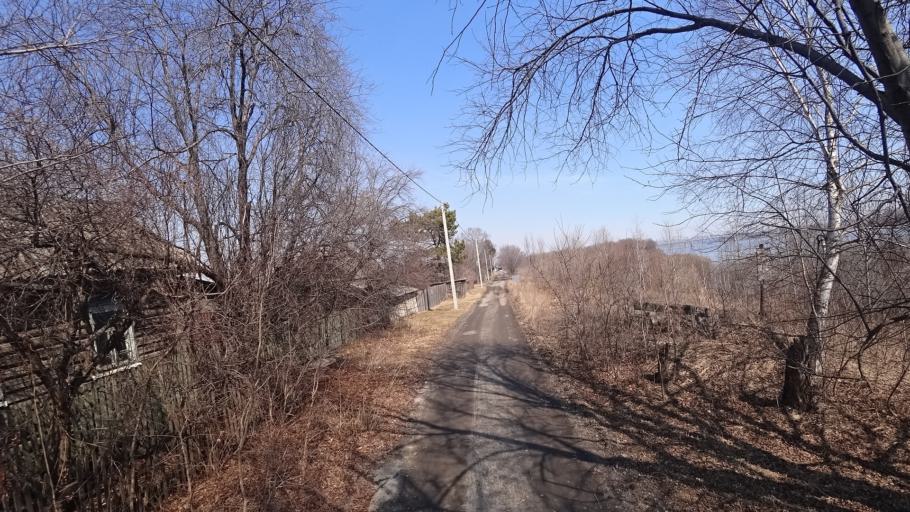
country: RU
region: Amur
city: Novobureyskiy
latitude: 49.7774
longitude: 129.8509
